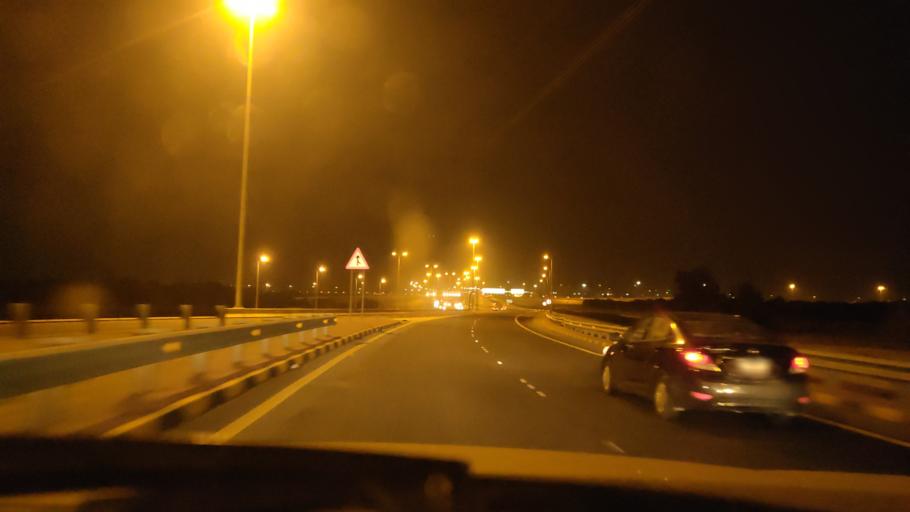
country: KW
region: Muhafazat al Jahra'
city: Al Jahra'
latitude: 29.2876
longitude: 47.7862
